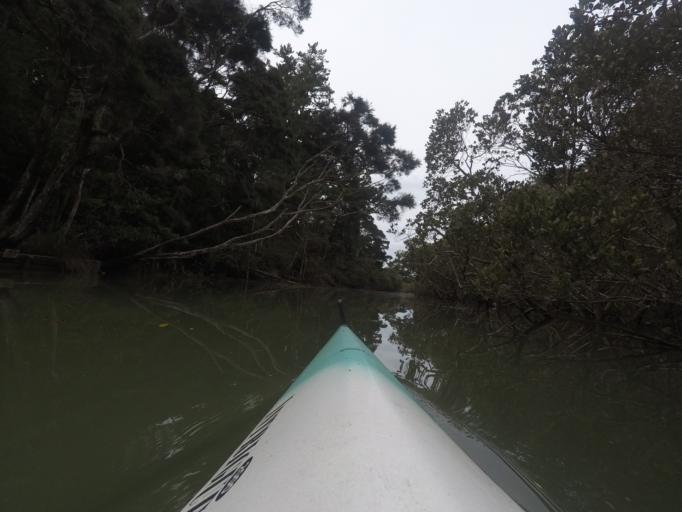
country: NZ
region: Auckland
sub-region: Auckland
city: Rothesay Bay
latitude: -36.6810
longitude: 174.7038
